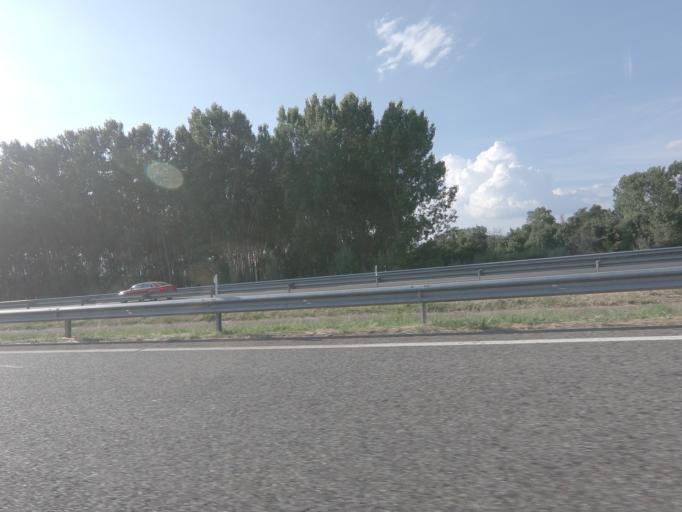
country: ES
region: Galicia
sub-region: Provincia de Ourense
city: Oimbra
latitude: 41.9225
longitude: -7.4727
